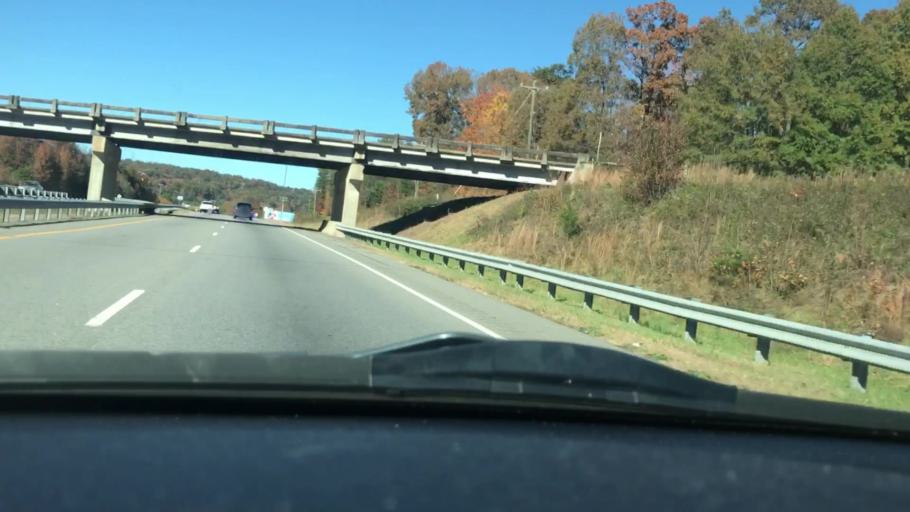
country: US
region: North Carolina
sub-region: Rockingham County
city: Mayodan
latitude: 36.4073
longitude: -79.9376
